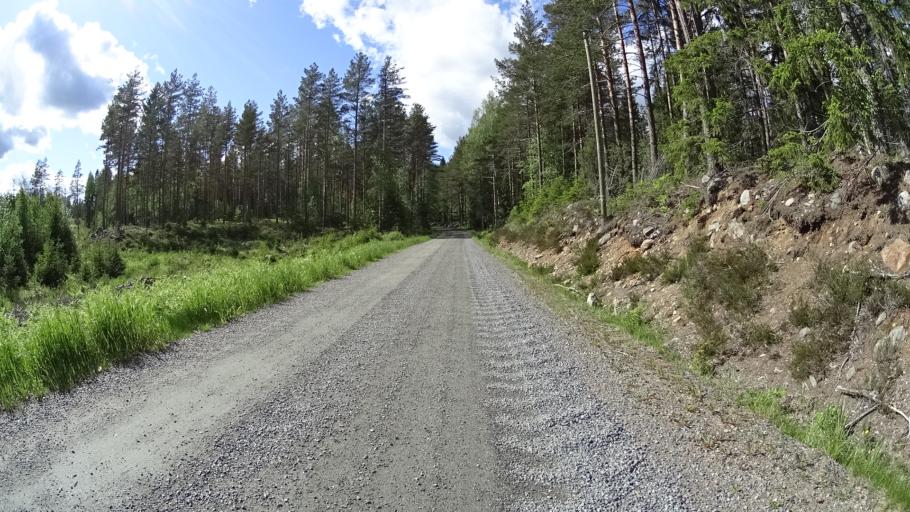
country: FI
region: Uusimaa
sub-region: Raaseporin
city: Pohja
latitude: 60.1843
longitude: 23.5818
